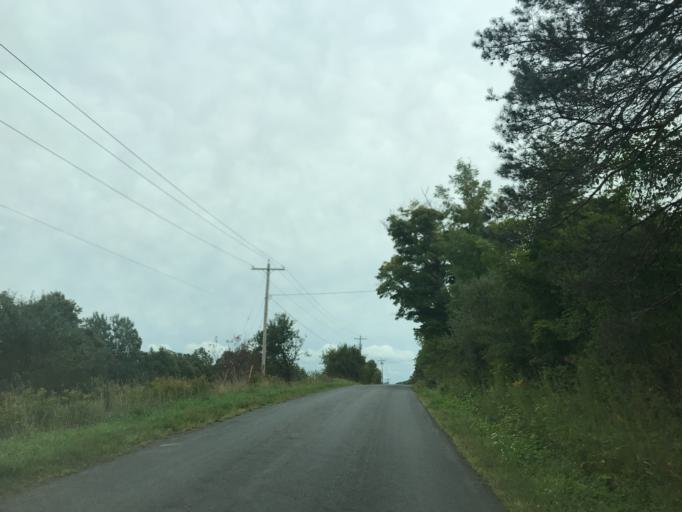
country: US
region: New York
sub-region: Otsego County
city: Worcester
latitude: 42.5725
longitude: -74.6715
